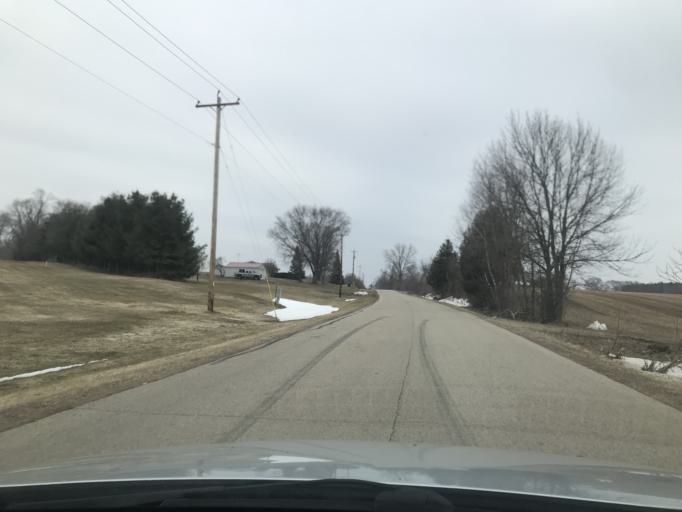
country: US
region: Wisconsin
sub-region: Marinette County
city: Peshtigo
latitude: 45.0387
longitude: -87.8618
